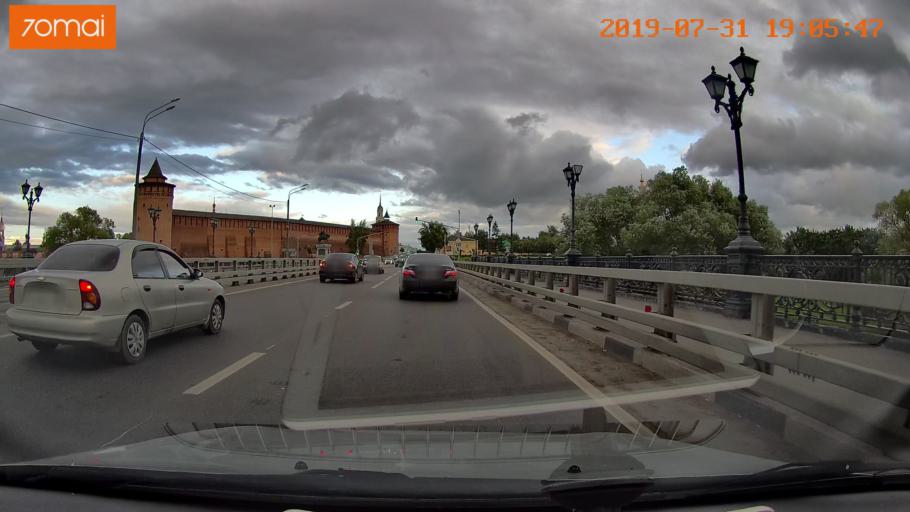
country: RU
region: Moskovskaya
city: Raduzhnyy
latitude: 55.1048
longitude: 38.7484
